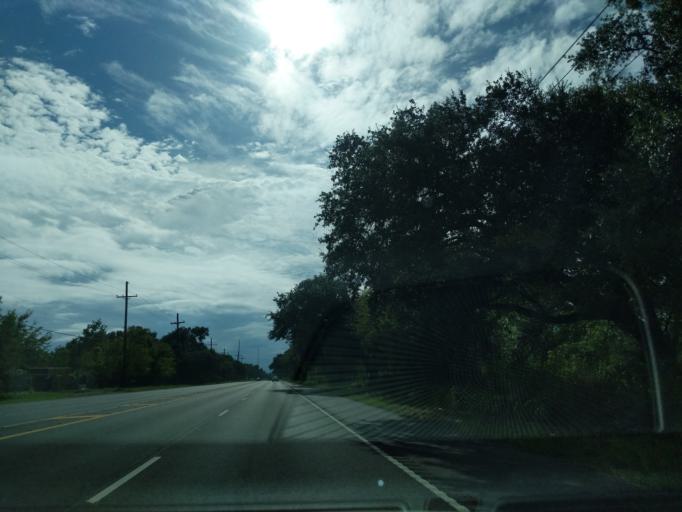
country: US
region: Louisiana
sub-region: Saint Bernard Parish
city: Meraux
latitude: 30.0544
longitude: -89.8767
